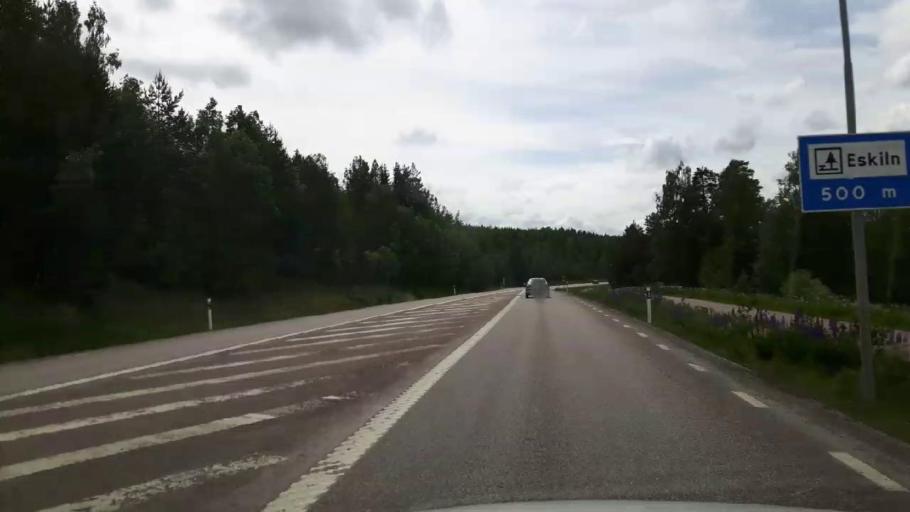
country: SE
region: Vaestmanland
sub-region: Fagersta Kommun
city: Fagersta
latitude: 59.9788
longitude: 15.7941
